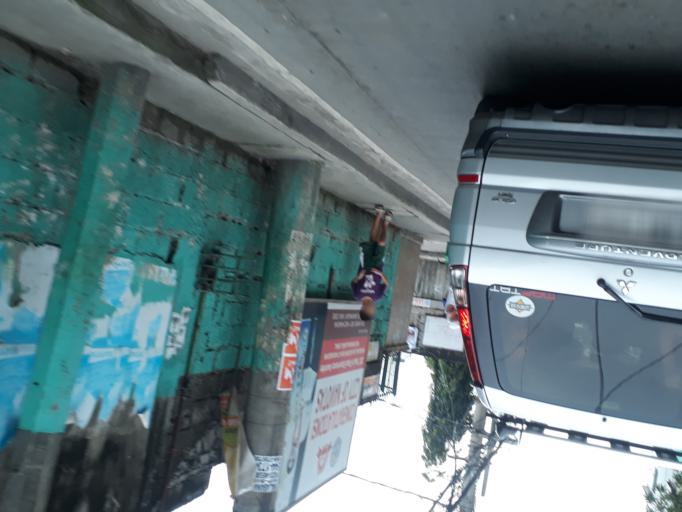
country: PH
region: Calabarzon
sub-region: Province of Rizal
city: Navotas
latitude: 14.6645
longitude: 120.9421
